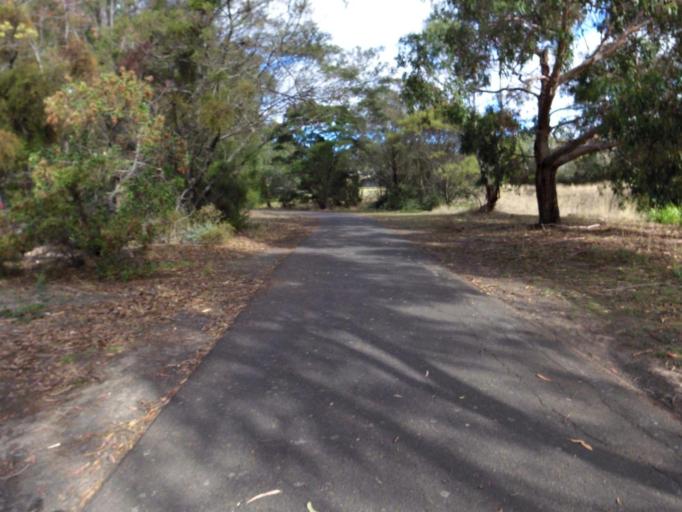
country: AU
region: Victoria
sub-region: Greater Geelong
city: Wandana Heights
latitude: -38.2047
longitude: 144.3069
